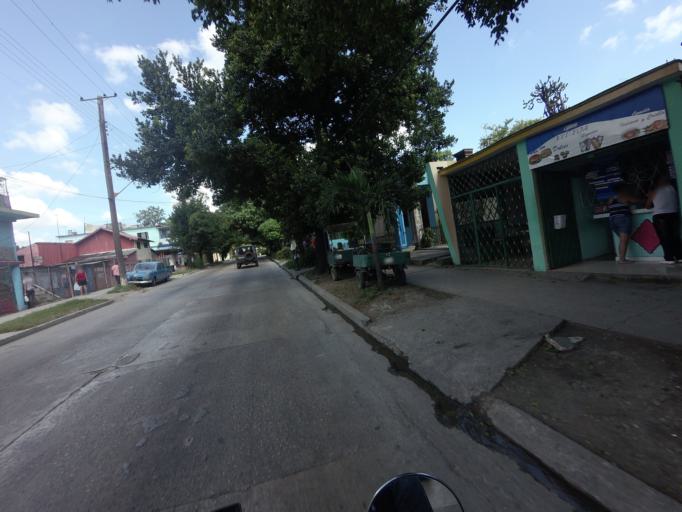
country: TM
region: Balkan
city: Gumdag
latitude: 38.8436
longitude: 54.1766
